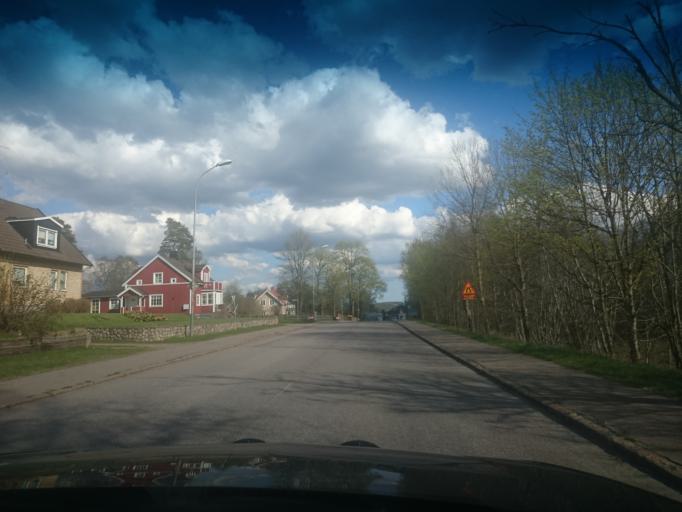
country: SE
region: Kronoberg
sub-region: Vaxjo Kommun
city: Braas
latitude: 57.1284
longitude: 15.1660
